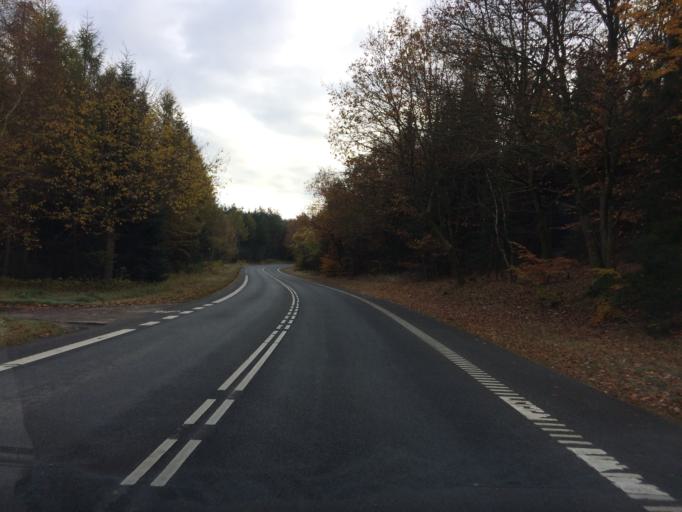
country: DK
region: Central Jutland
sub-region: Silkeborg Kommune
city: Virklund
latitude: 56.1532
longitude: 9.5716
